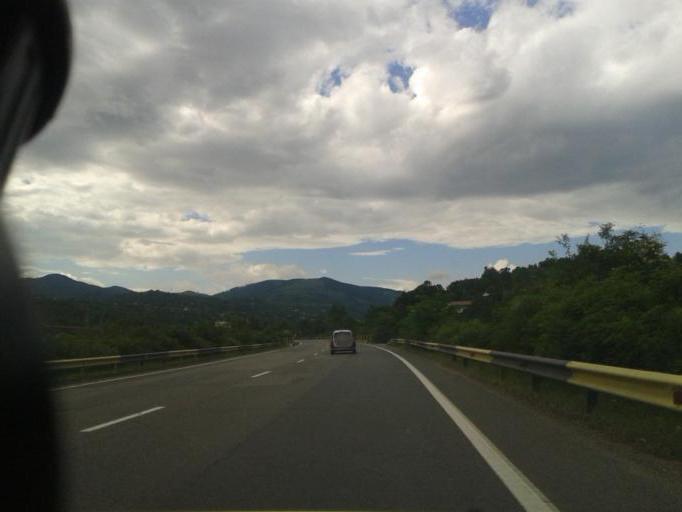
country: RO
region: Prahova
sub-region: Oras Breaza
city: Gura Beliei
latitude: 45.2208
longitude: 25.6451
